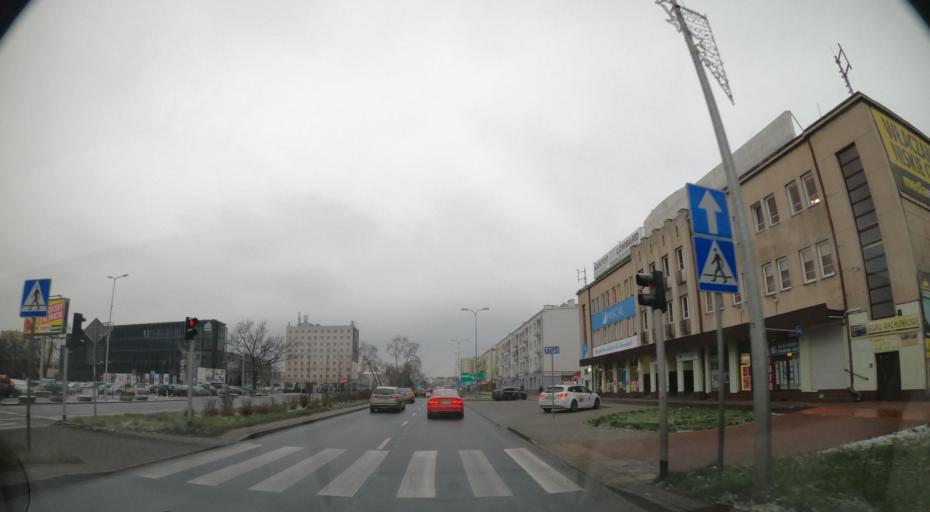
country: PL
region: Masovian Voivodeship
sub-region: Plock
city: Plock
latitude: 52.5492
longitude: 19.6943
